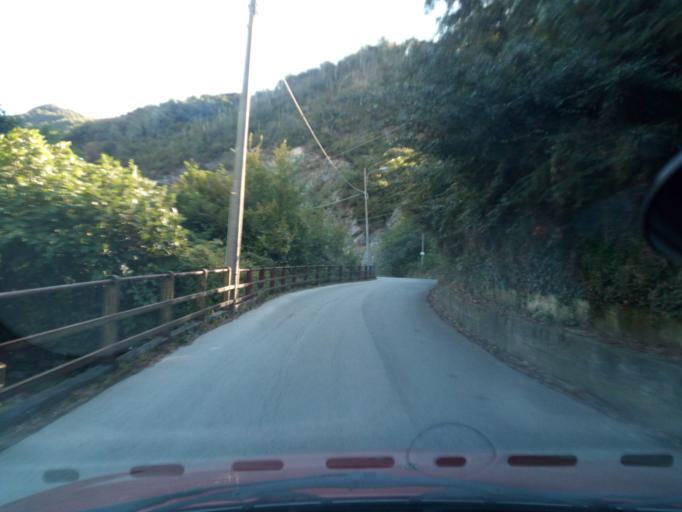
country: IT
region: Liguria
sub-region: Provincia di Genova
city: Isoverde
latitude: 44.4797
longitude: 8.8350
